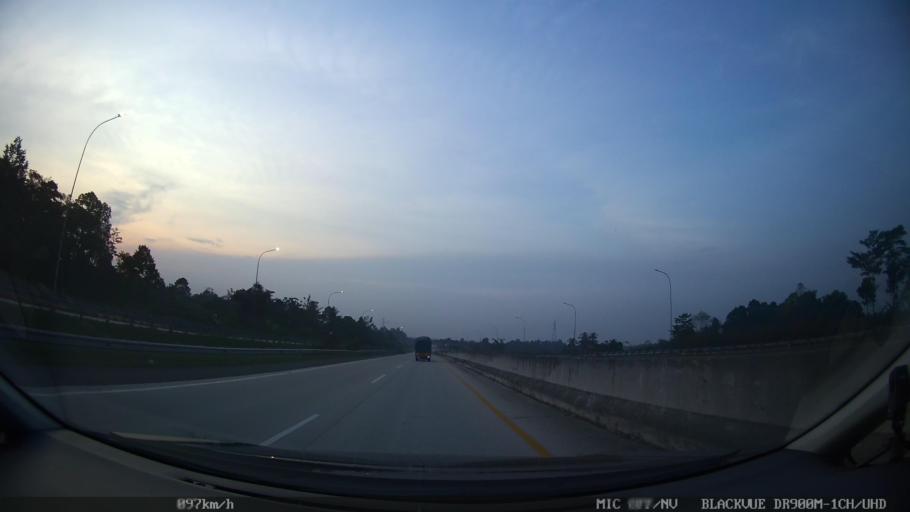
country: ID
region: Lampung
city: Pasuruan
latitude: -5.7255
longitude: 105.6676
